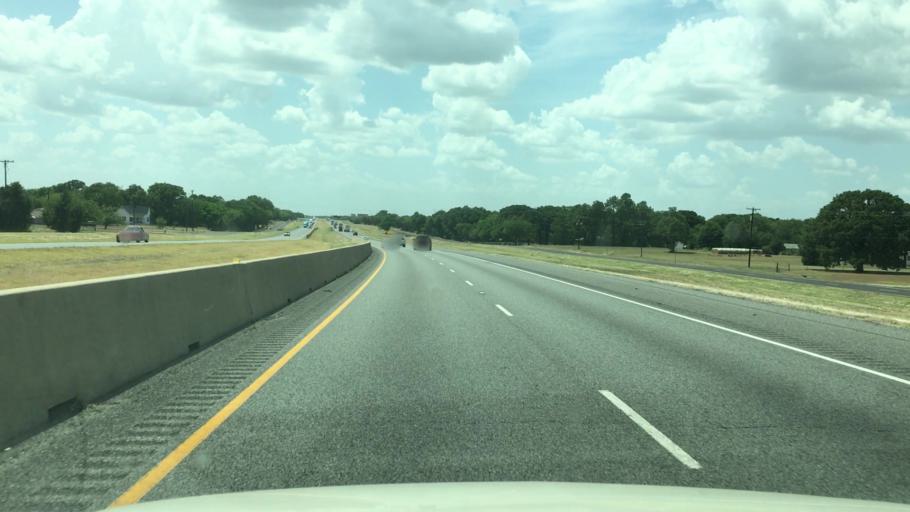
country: US
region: Texas
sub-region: Hunt County
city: Greenville
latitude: 33.1326
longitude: -96.0144
